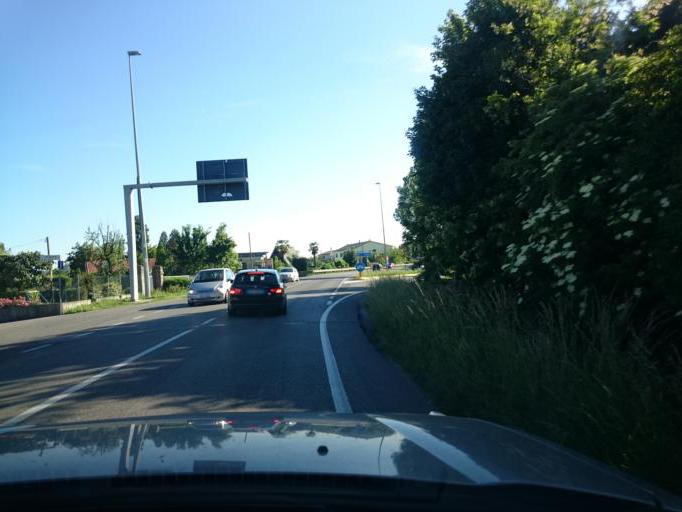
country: IT
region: Veneto
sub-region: Provincia di Venezia
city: Noale
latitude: 45.5426
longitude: 12.0697
